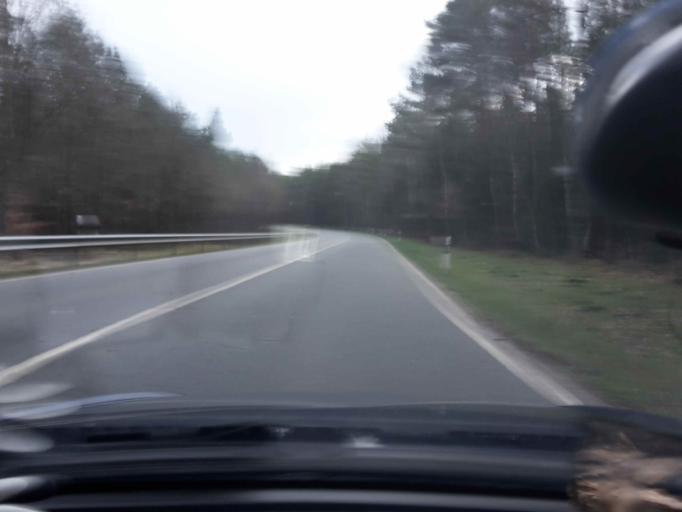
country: DE
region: Lower Saxony
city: Bispingen
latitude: 53.0471
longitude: 10.0495
